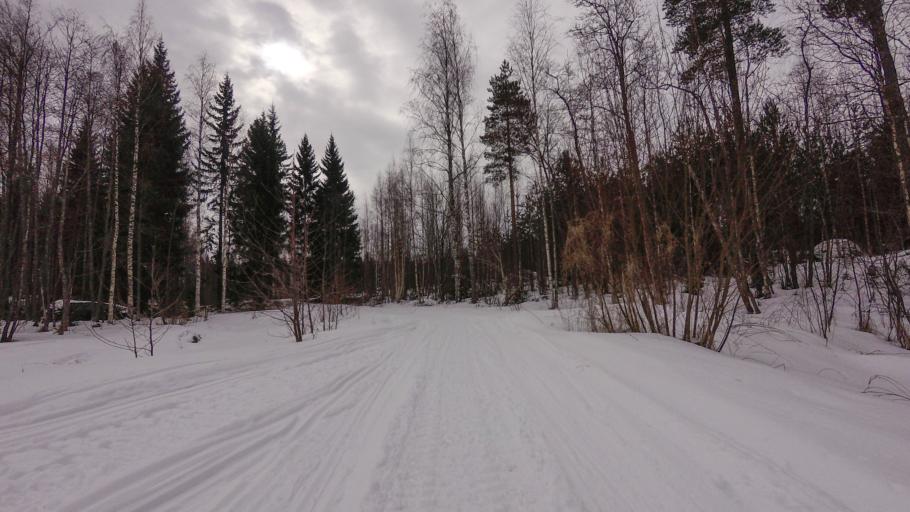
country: FI
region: Southern Savonia
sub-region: Savonlinna
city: Enonkoski
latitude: 62.1199
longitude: 28.6229
